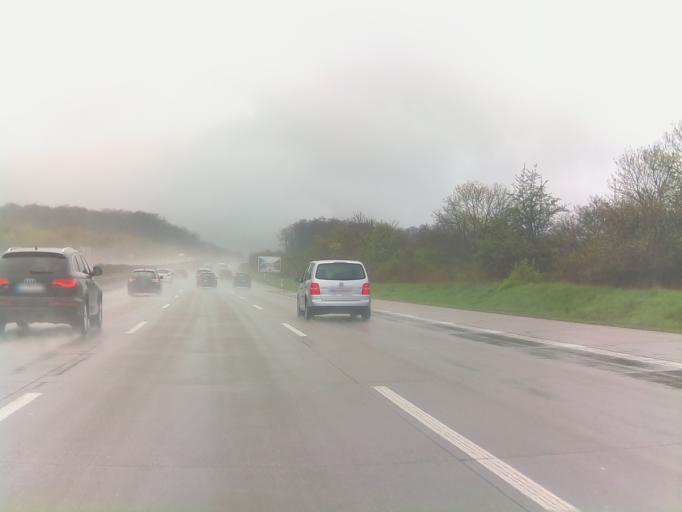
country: DE
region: Thuringia
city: Klettbach
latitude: 50.9217
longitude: 11.1169
